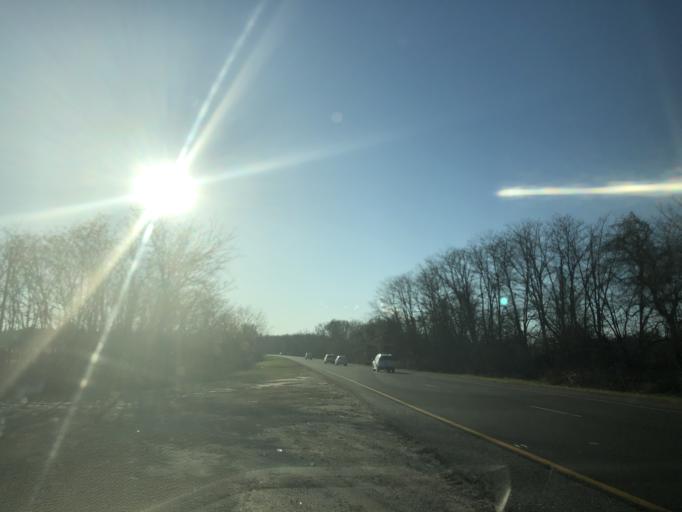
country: US
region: New Jersey
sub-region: Salem County
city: Carneys Point
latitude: 39.7029
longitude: -75.4570
